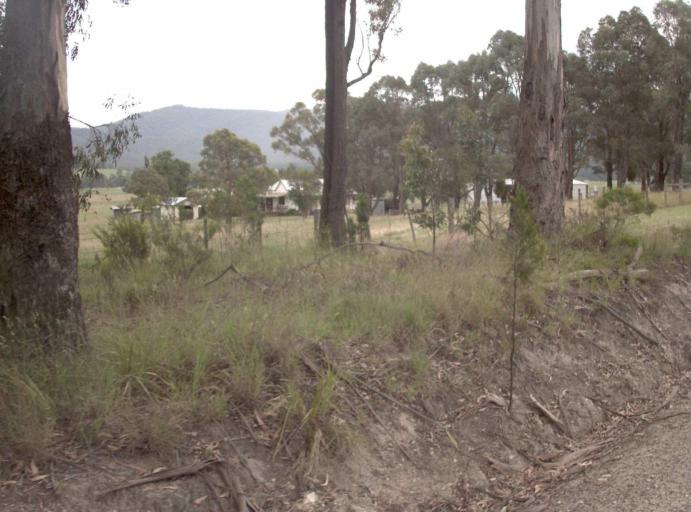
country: AU
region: New South Wales
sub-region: Bombala
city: Bombala
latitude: -37.4949
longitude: 149.1813
